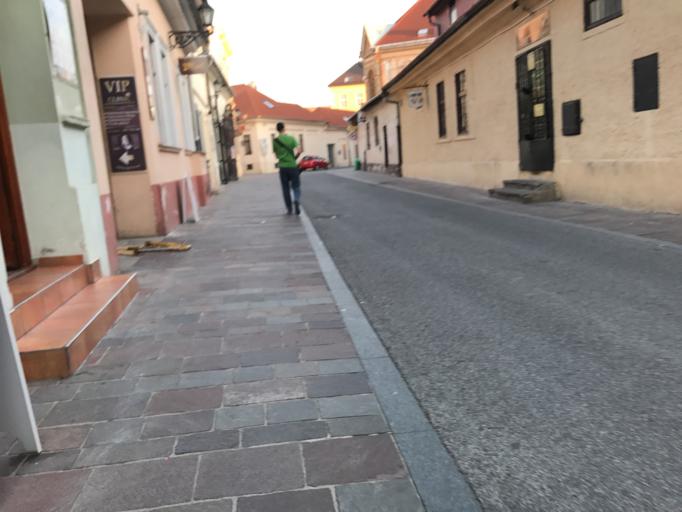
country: SK
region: Kosicky
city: Kosice
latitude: 48.7191
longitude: 21.2568
